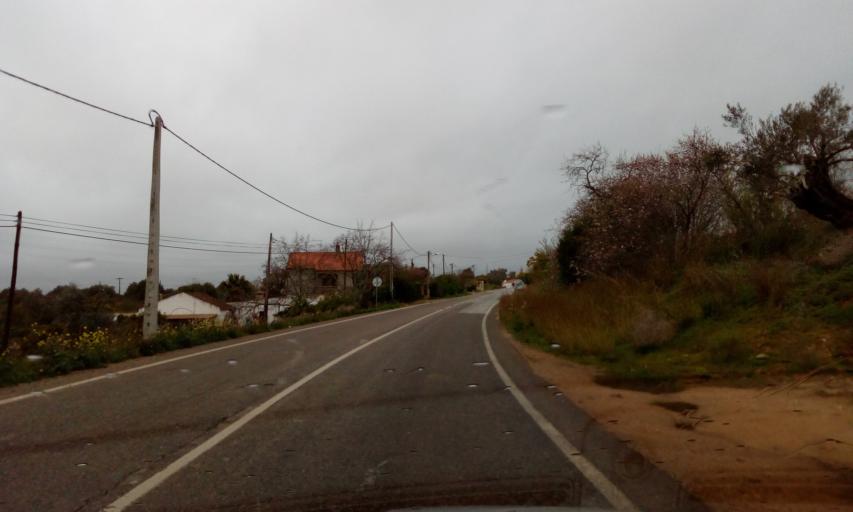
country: PT
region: Faro
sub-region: Albufeira
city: Guia
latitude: 37.1718
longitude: -8.3346
